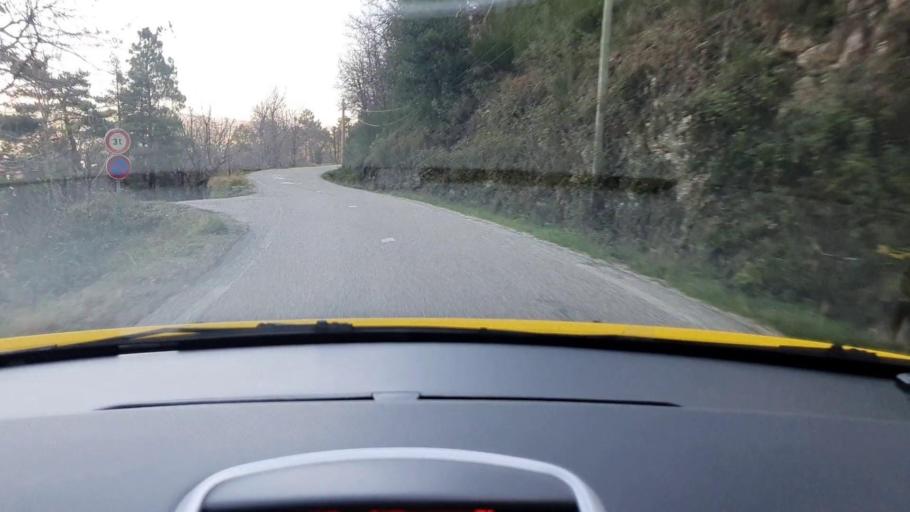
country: FR
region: Languedoc-Roussillon
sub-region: Departement du Gard
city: Branoux-les-Taillades
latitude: 44.2837
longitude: 3.9692
